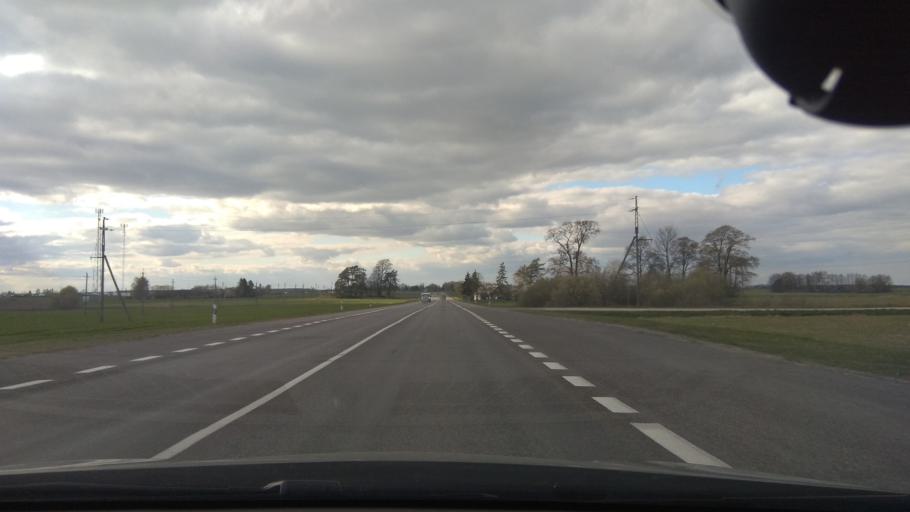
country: LT
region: Siauliu apskritis
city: Pakruojis
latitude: 55.7882
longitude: 24.0348
